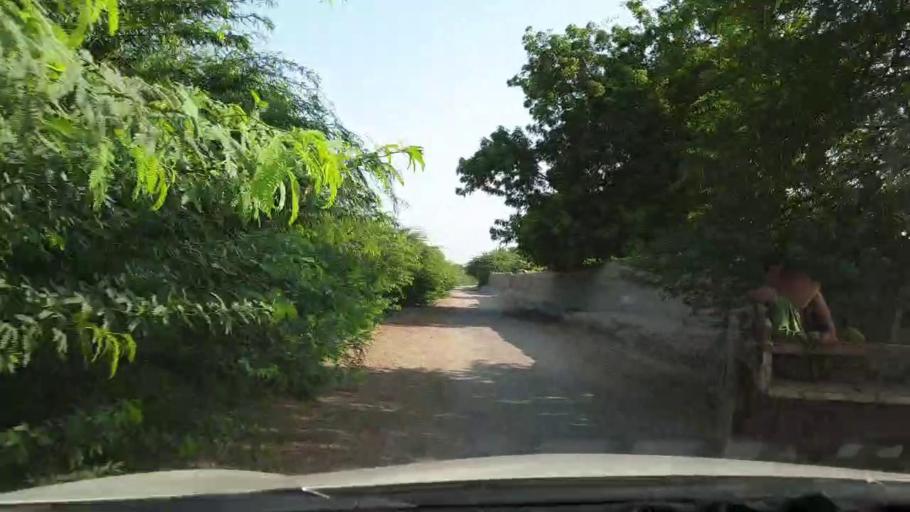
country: PK
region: Sindh
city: Larkana
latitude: 27.5564
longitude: 68.2569
